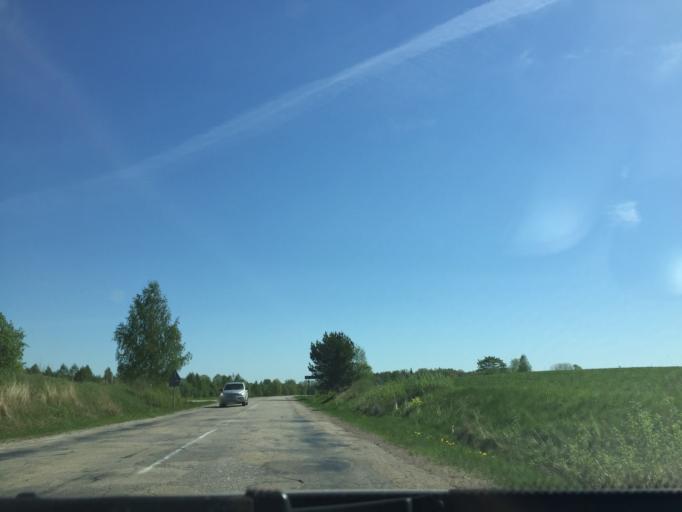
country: LV
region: Incukalns
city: Incukalns
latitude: 57.0267
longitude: 24.7958
